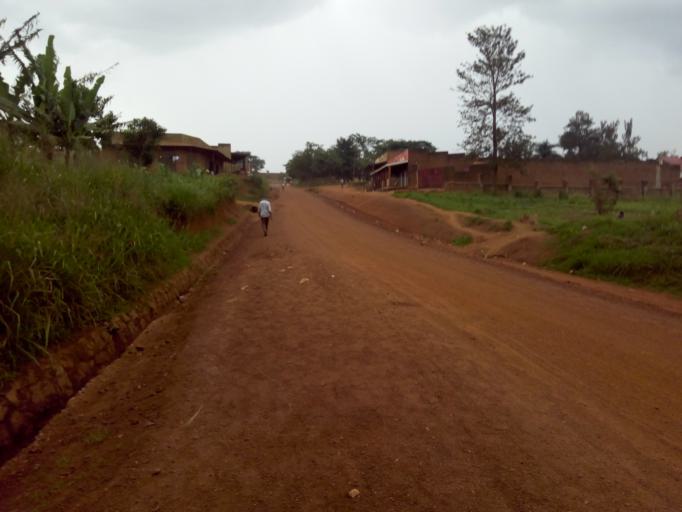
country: UG
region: Western Region
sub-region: Masindi District
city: Masindi
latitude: 1.6792
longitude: 31.7166
